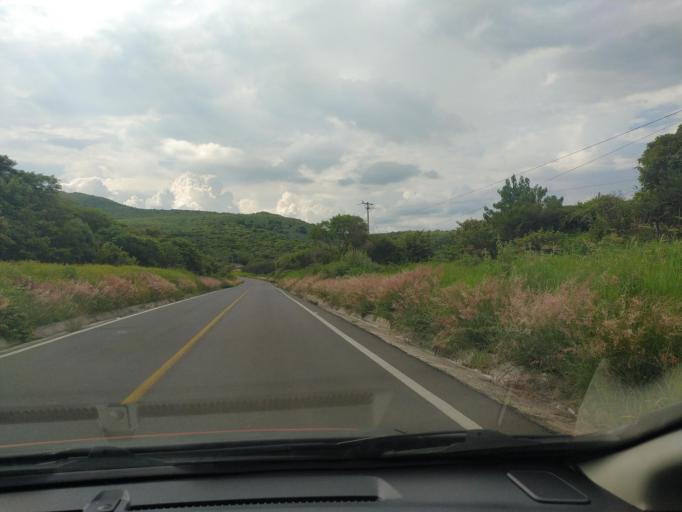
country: MX
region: Jalisco
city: Villa Corona
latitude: 20.4029
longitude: -103.6819
